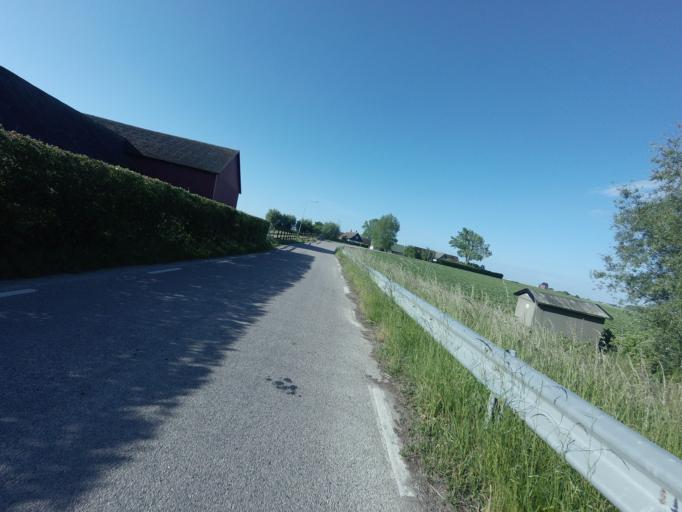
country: SE
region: Skane
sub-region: Malmo
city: Oxie
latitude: 55.4569
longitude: 13.1226
